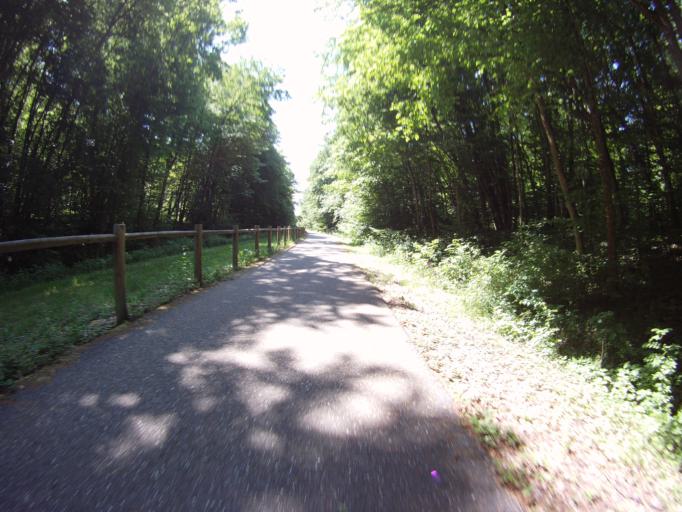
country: FR
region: Lorraine
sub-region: Departement de Meurthe-et-Moselle
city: Champenoux
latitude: 48.7519
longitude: 6.3249
